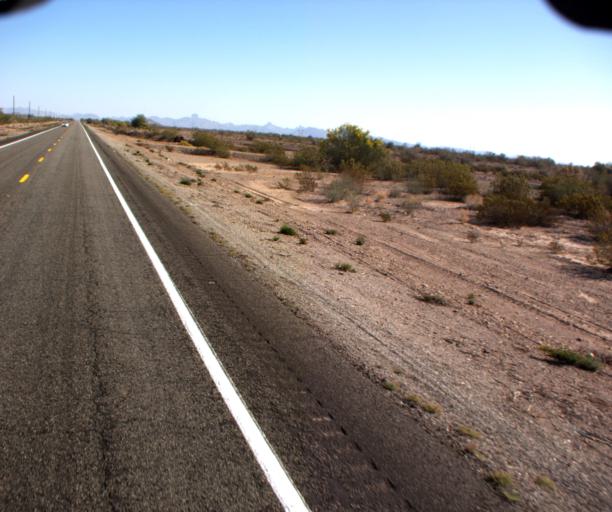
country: US
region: Arizona
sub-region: Yuma County
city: Fortuna Foothills
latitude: 32.8783
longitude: -114.3483
